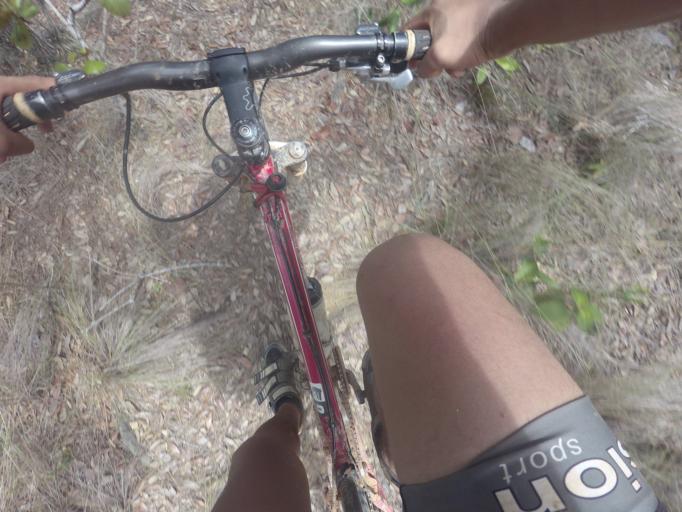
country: CU
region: Pinar del Rio
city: Vinales
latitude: 22.5798
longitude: -83.7714
